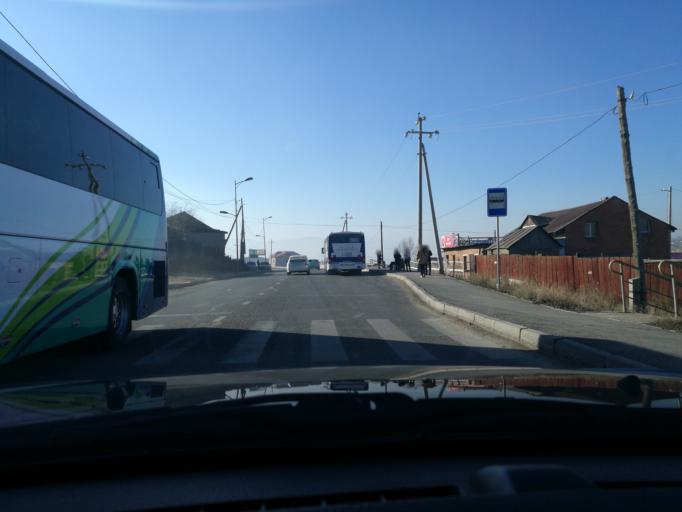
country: MN
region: Ulaanbaatar
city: Ulaanbaatar
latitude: 47.9716
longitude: 106.9307
